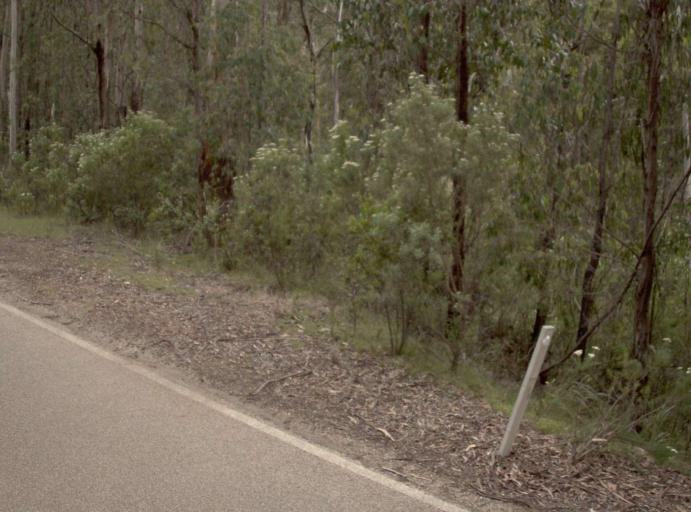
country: AU
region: Victoria
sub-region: East Gippsland
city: Bairnsdale
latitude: -37.6245
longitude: 147.1957
